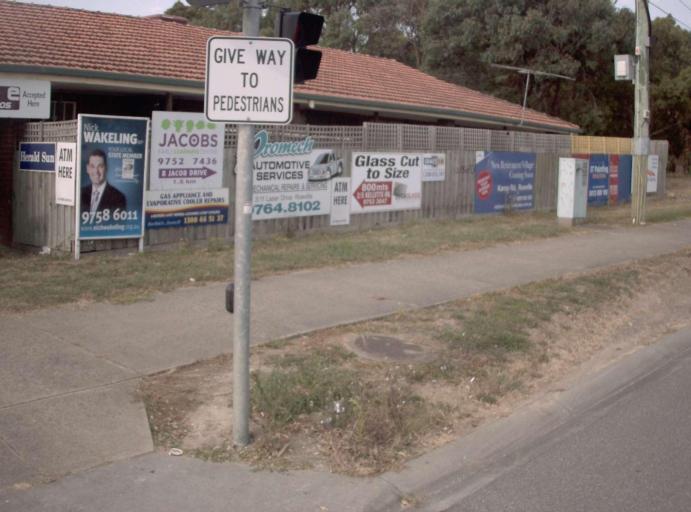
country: AU
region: Victoria
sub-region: Knox
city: Scoresby
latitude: -37.9118
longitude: 145.2473
